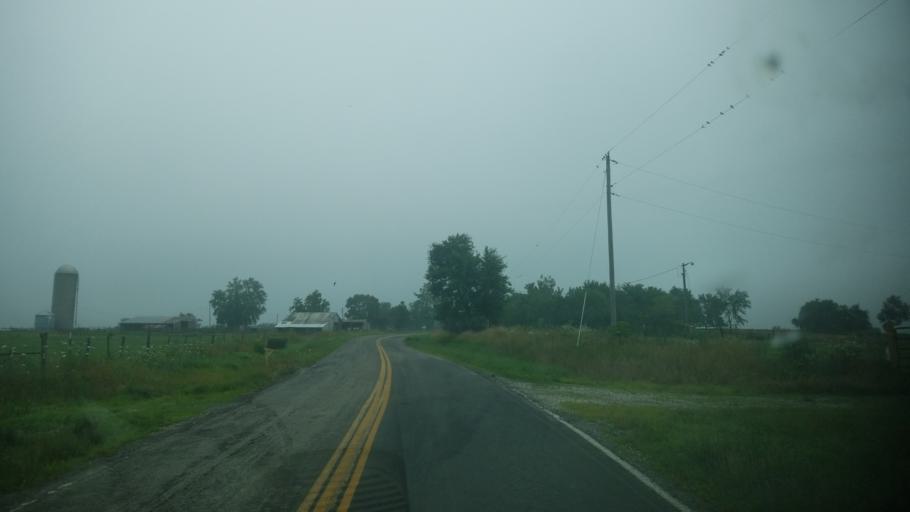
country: US
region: Missouri
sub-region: Audrain County
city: Vandalia
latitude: 39.2755
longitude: -91.3466
